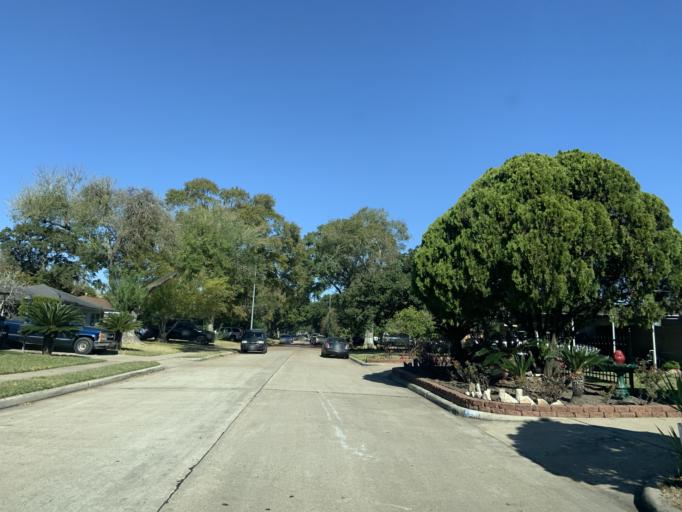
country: US
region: Texas
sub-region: Harris County
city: Bellaire
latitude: 29.6811
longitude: -95.5109
